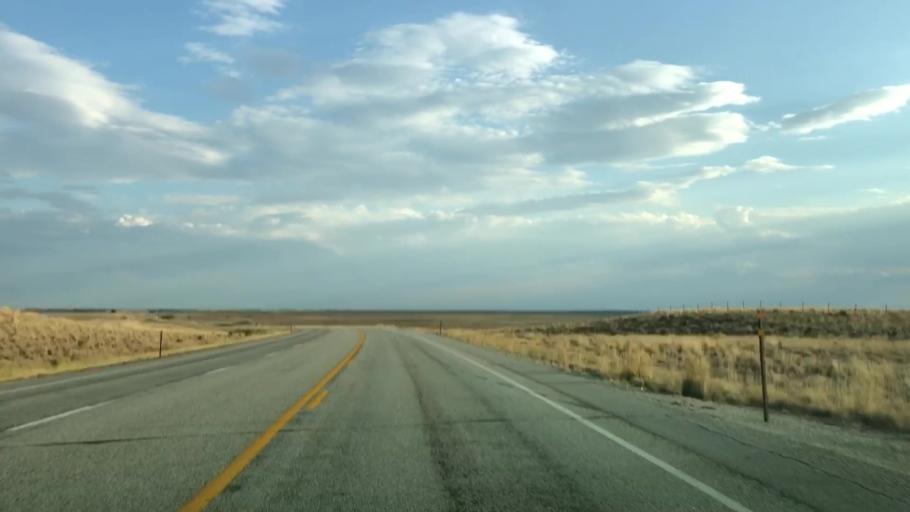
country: US
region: Wyoming
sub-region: Sweetwater County
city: North Rock Springs
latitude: 42.1923
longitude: -109.4812
